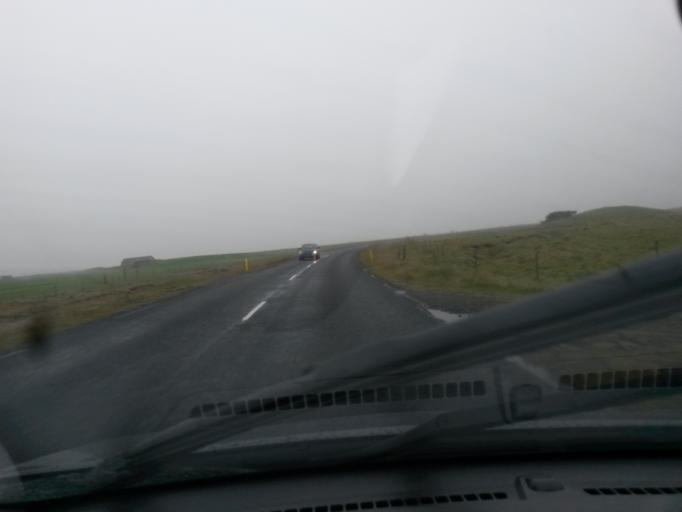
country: IS
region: South
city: Vestmannaeyjar
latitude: 63.4329
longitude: -19.1884
